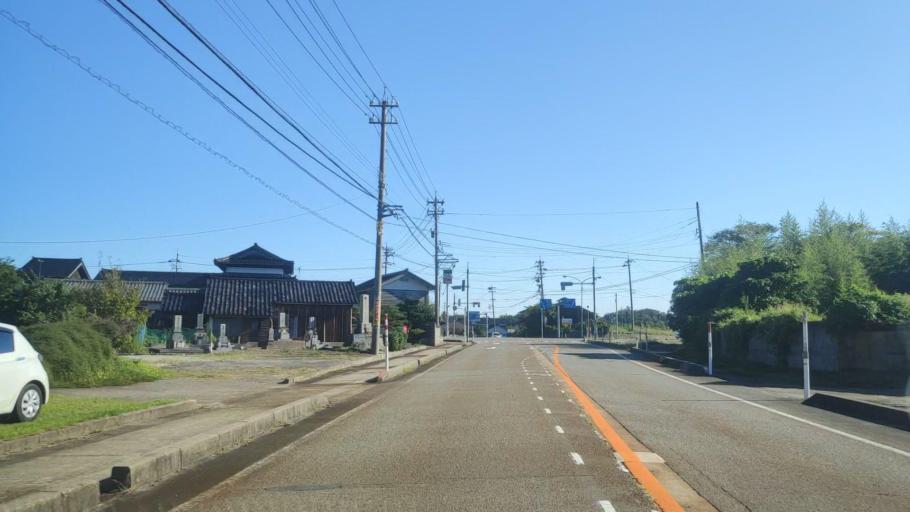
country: JP
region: Ishikawa
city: Hakui
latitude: 36.8433
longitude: 136.7656
